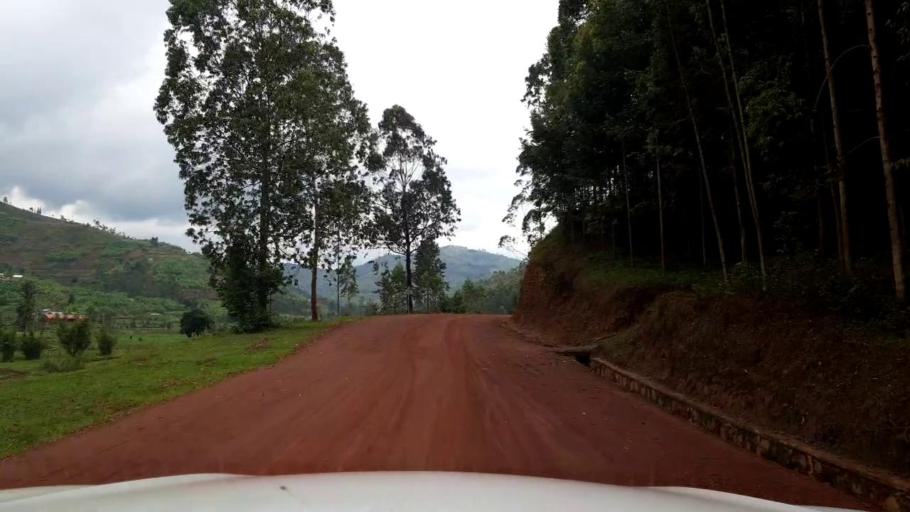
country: RW
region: Northern Province
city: Musanze
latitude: -1.6736
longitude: 29.7984
